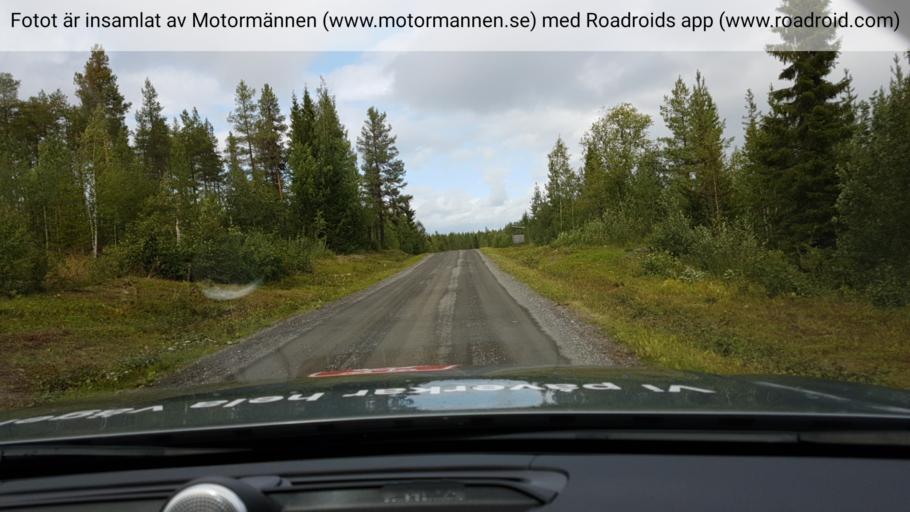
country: SE
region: Jaemtland
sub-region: OEstersunds Kommun
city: Lit
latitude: 63.7534
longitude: 14.6526
